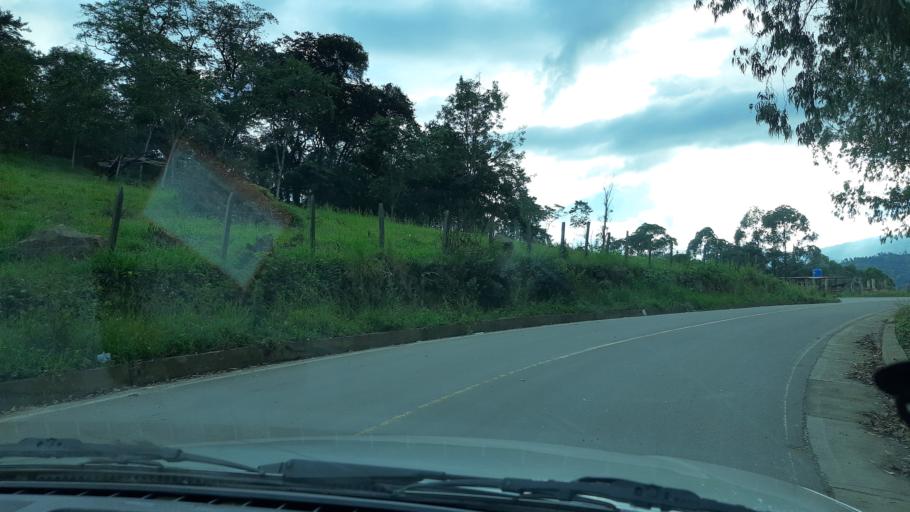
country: CO
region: Boyaca
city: Garagoa
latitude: 5.0913
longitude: -73.3655
